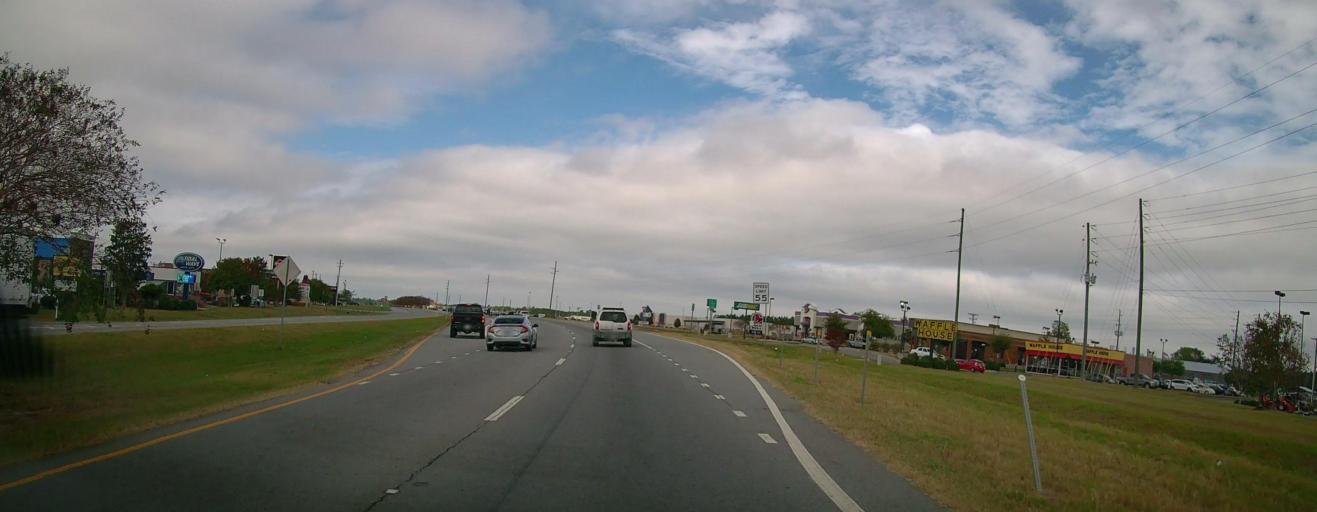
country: US
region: Georgia
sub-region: Colquitt County
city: Moultrie
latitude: 31.1894
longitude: -83.7618
